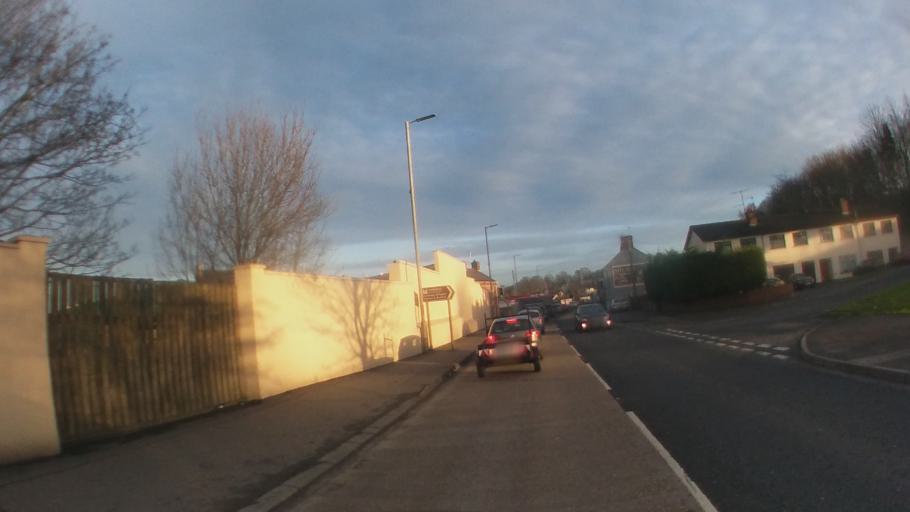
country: GB
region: Northern Ireland
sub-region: Armagh District
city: Armagh
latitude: 54.3556
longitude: -6.6596
